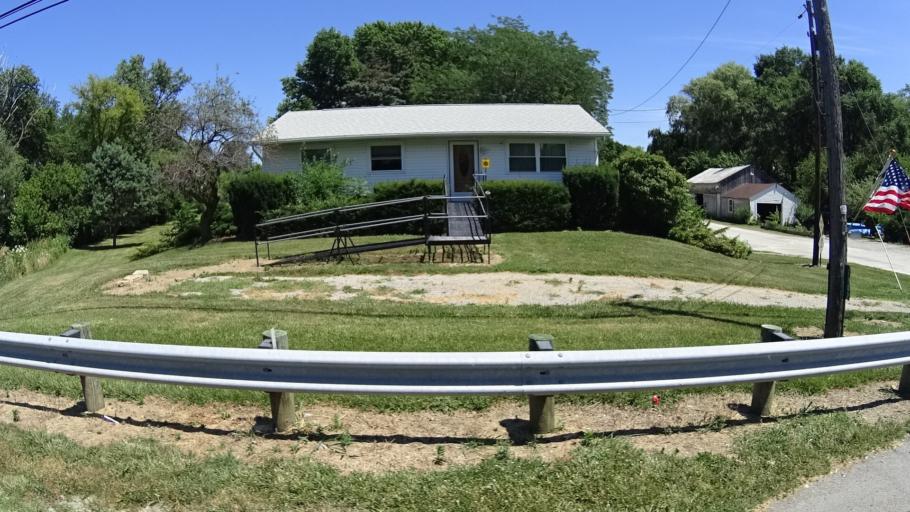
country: US
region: Ohio
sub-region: Erie County
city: Sandusky
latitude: 41.4258
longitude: -82.7039
